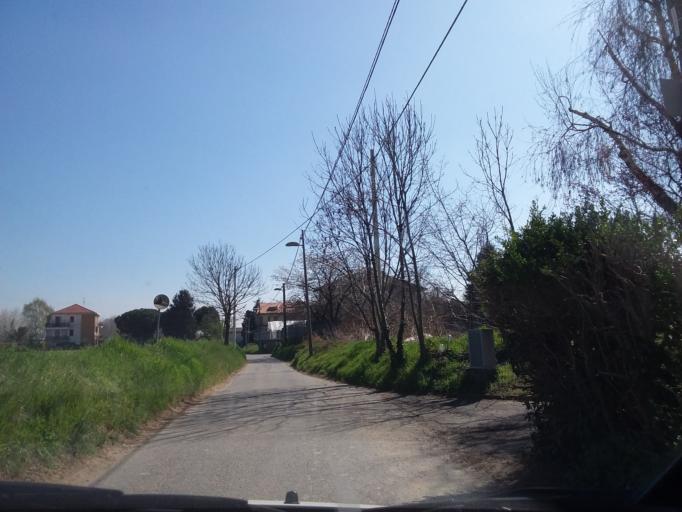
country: IT
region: Piedmont
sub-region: Provincia di Torino
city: Rivoli
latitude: 45.0585
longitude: 7.5082
